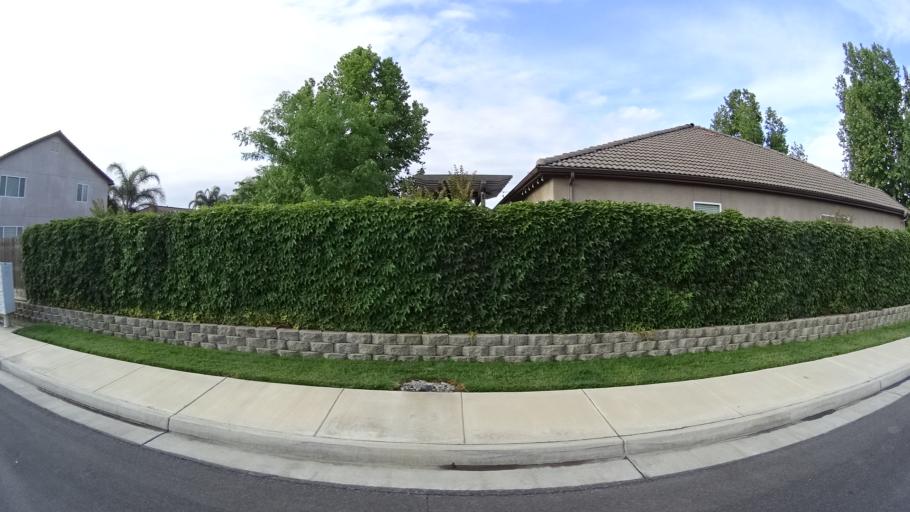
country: US
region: California
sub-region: Kings County
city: Hanford
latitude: 36.3469
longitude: -119.6752
